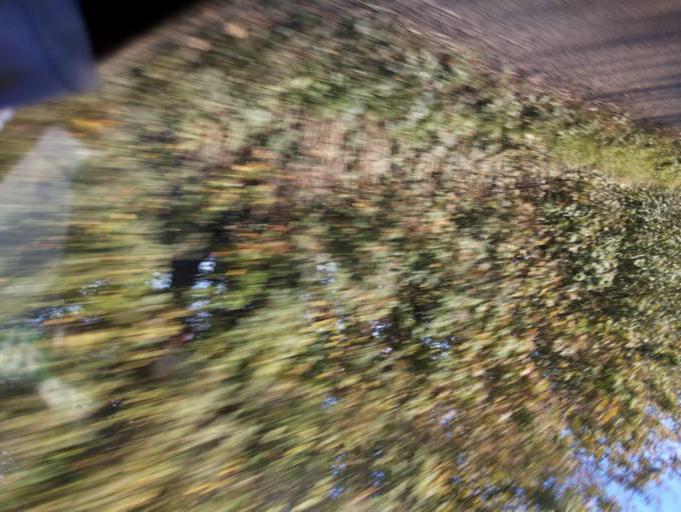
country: GB
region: England
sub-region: Herefordshire
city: Ledbury
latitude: 52.0505
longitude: -2.4772
